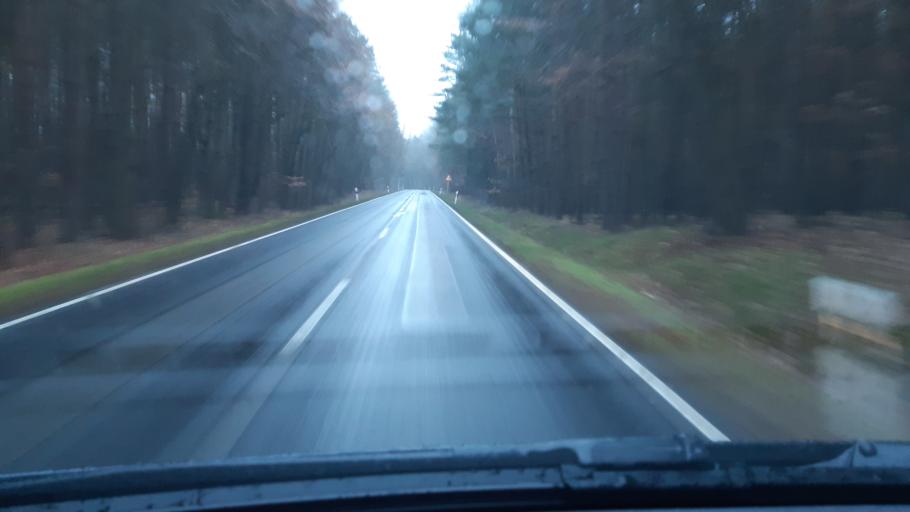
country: DE
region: Brandenburg
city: Milmersdorf
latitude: 53.1586
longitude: 13.6042
